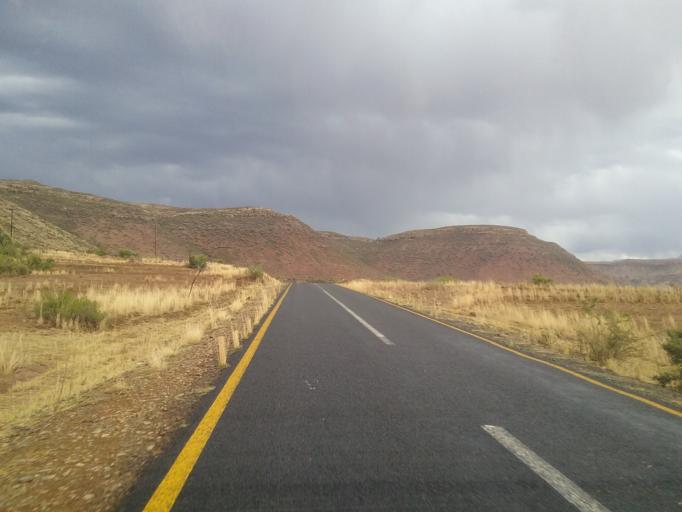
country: LS
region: Quthing
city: Quthing
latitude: -30.3462
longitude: 27.7201
